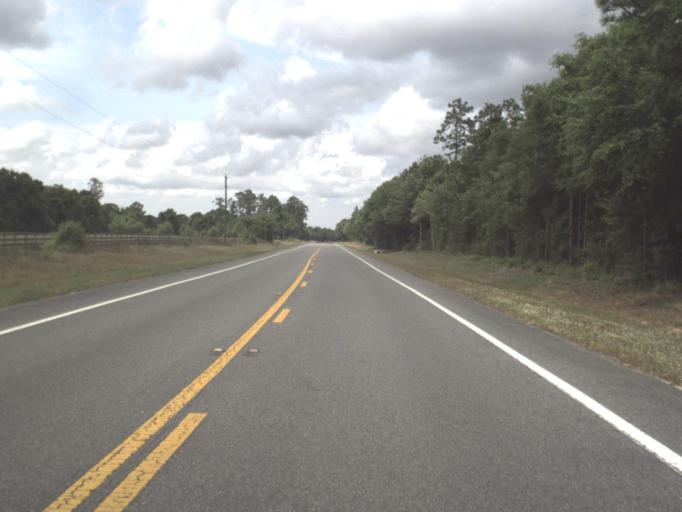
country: US
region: Florida
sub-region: Santa Rosa County
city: Point Baker
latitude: 30.7264
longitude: -87.0814
